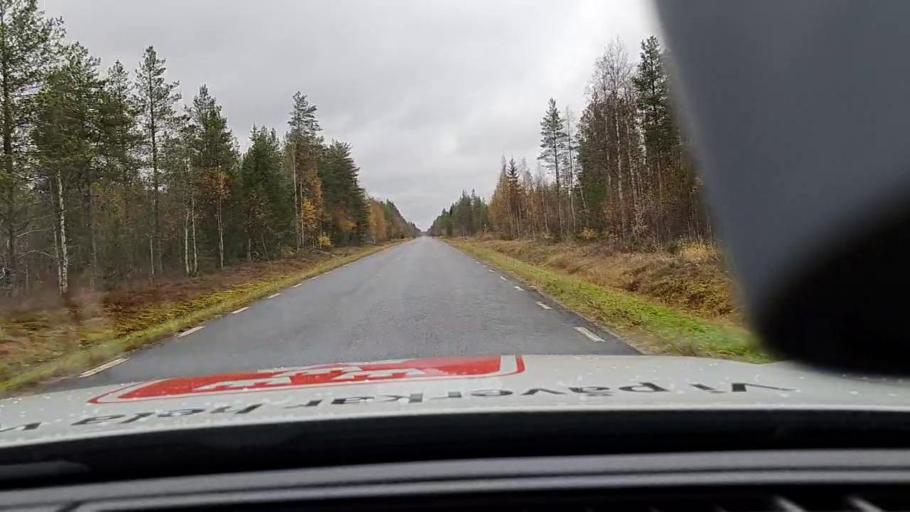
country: SE
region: Norrbotten
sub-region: Haparanda Kommun
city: Haparanda
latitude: 65.9081
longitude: 23.8312
